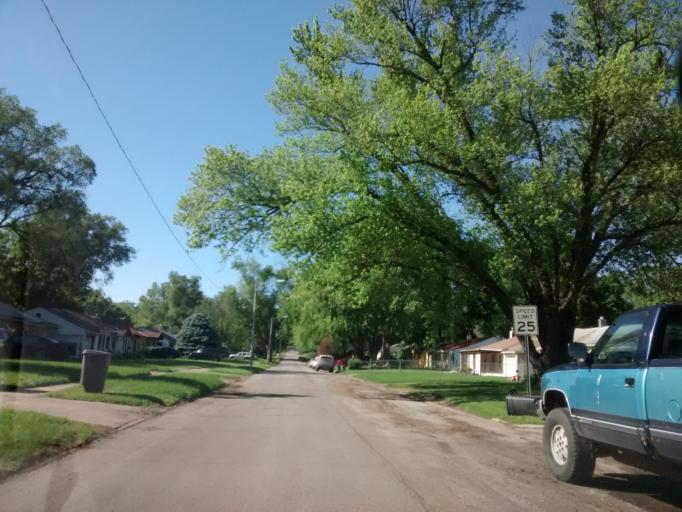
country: US
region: Nebraska
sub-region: Douglas County
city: Ralston
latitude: 41.2528
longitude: -96.0200
